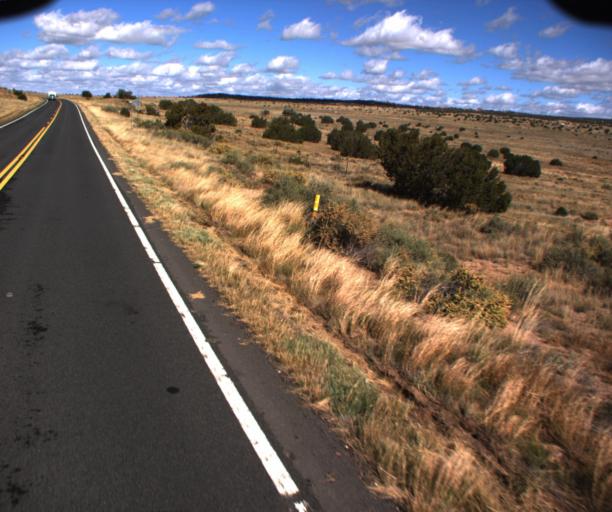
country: US
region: Arizona
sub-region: Apache County
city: Houck
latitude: 35.0243
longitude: -109.2452
